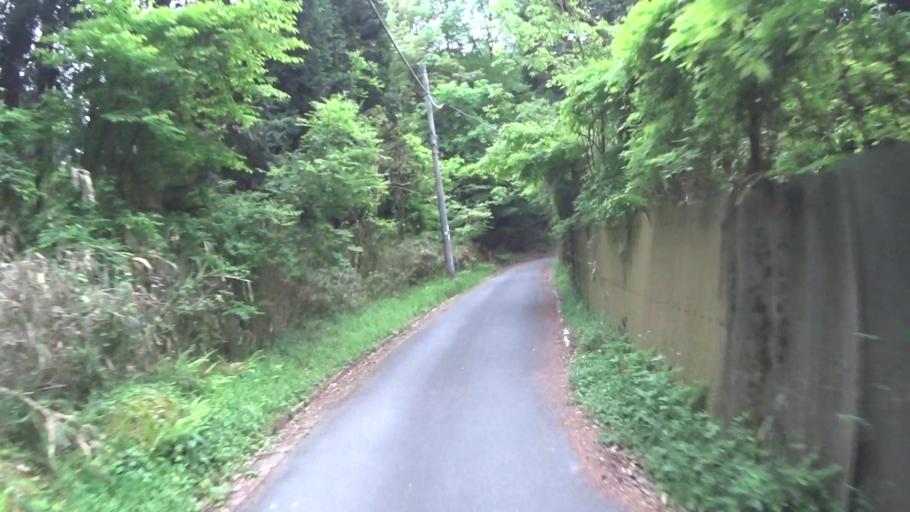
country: JP
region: Kyoto
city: Kameoka
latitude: 35.0617
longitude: 135.5362
